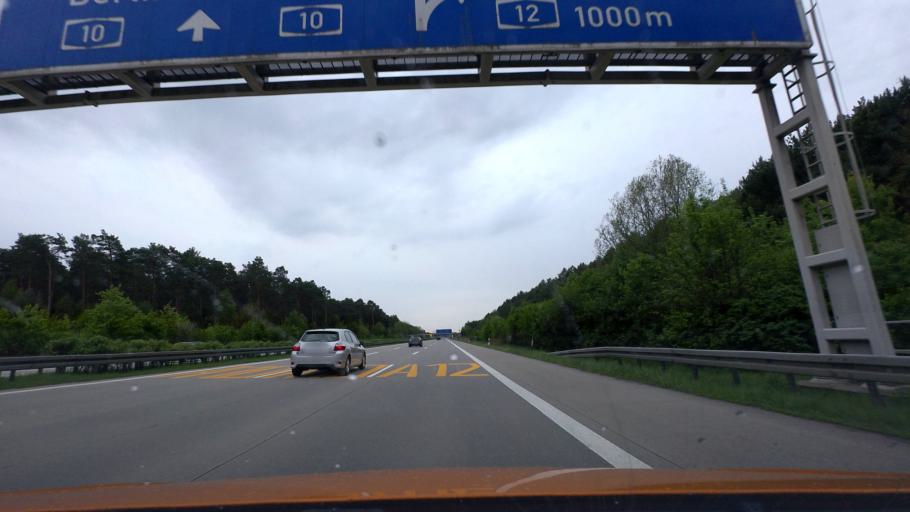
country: DE
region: Brandenburg
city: Erkner
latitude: 52.3414
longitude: 13.7543
